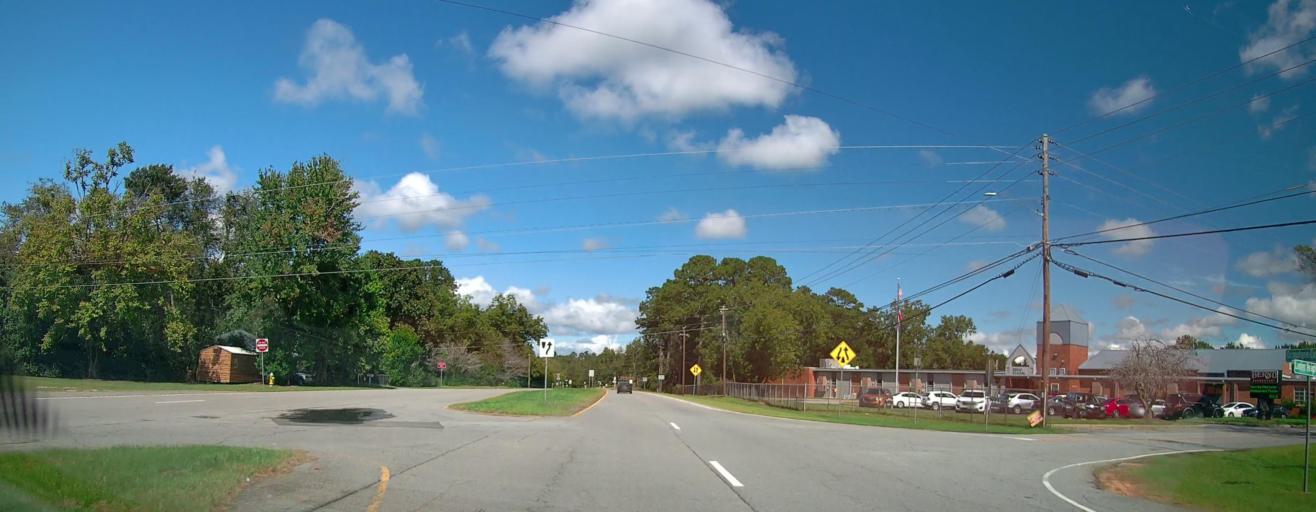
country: US
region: Georgia
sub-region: Bibb County
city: Macon
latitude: 32.8130
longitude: -83.5689
